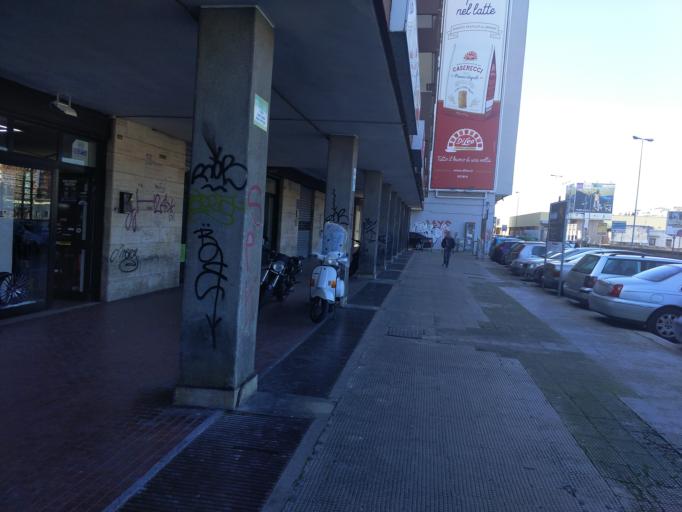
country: IT
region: Apulia
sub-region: Provincia di Bari
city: Bari
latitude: 41.1166
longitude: 16.8637
